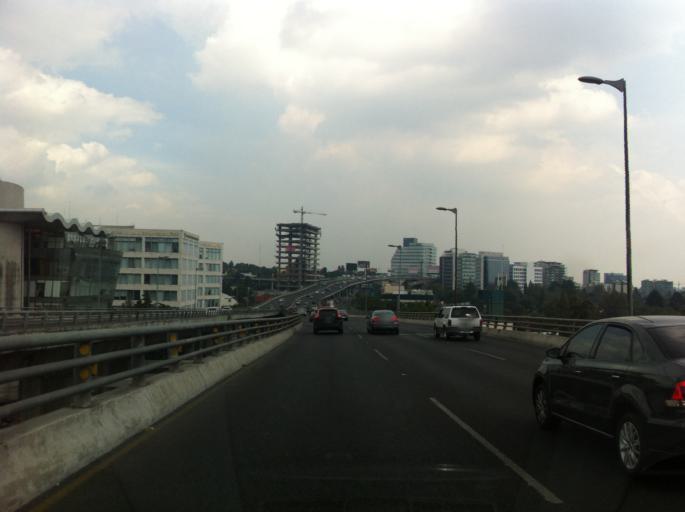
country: MX
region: Mexico City
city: Alvaro Obregon
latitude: 19.3498
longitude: -99.2011
